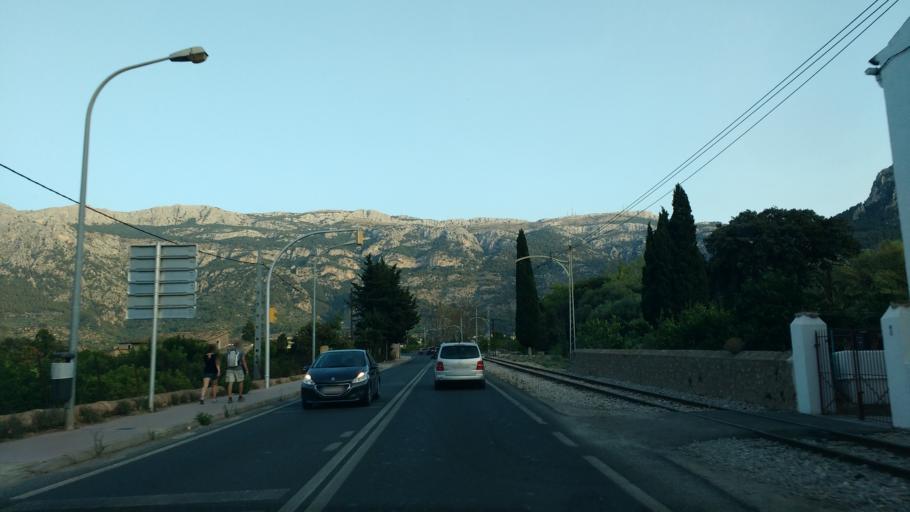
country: ES
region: Balearic Islands
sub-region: Illes Balears
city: Soller
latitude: 39.7819
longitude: 2.7003
